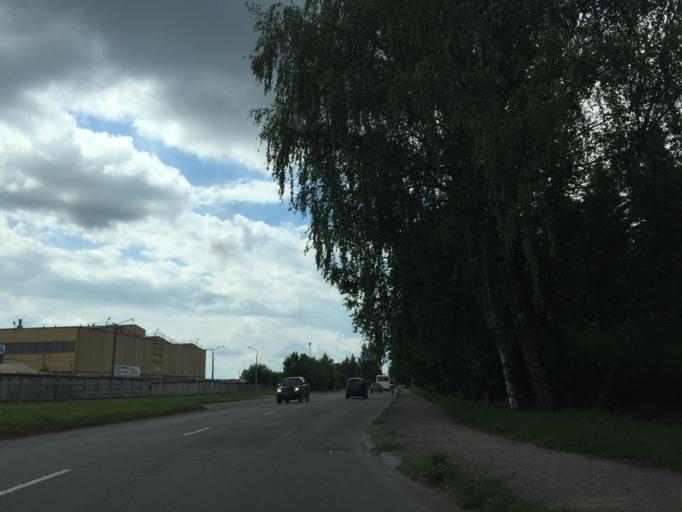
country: LV
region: Ozolnieku
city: Ozolnieki
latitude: 56.6618
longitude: 23.7672
